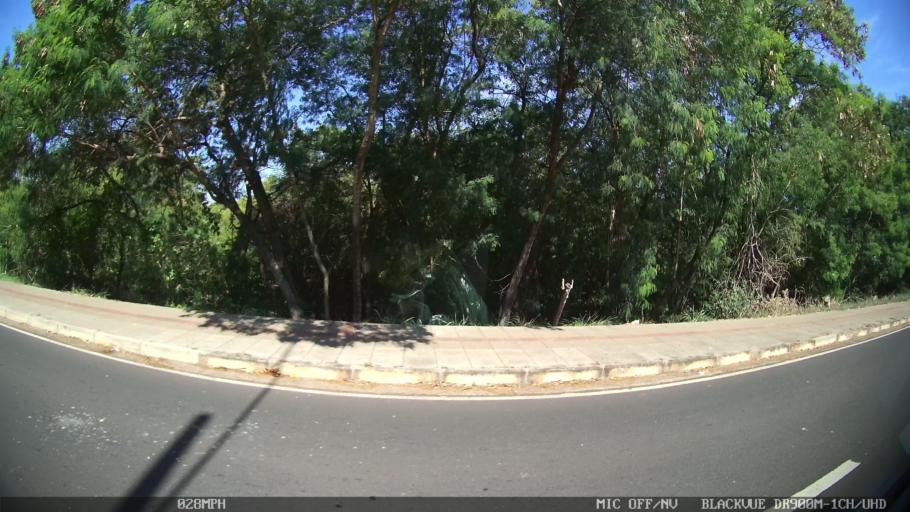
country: BR
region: Sao Paulo
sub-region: Sao Jose Do Rio Preto
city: Sao Jose do Rio Preto
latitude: -20.7775
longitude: -49.3882
